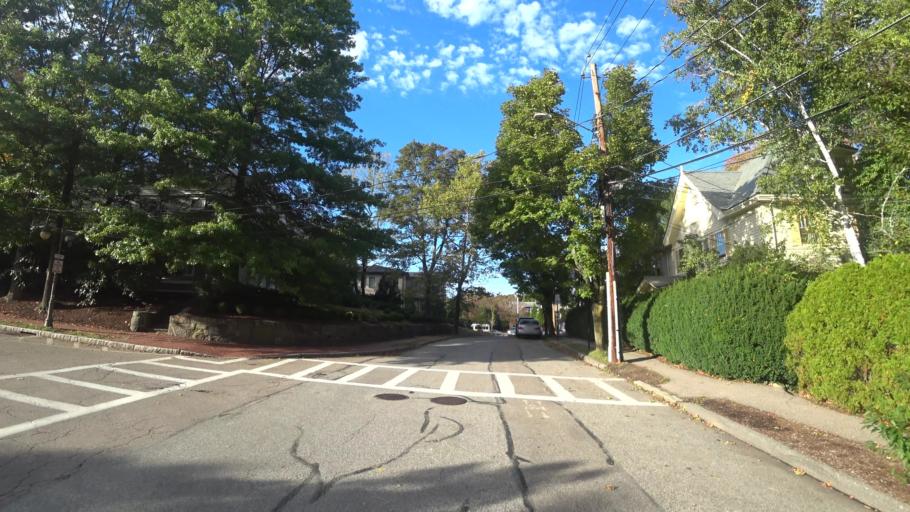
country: US
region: Massachusetts
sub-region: Norfolk County
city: Brookline
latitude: 42.3288
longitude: -71.1284
